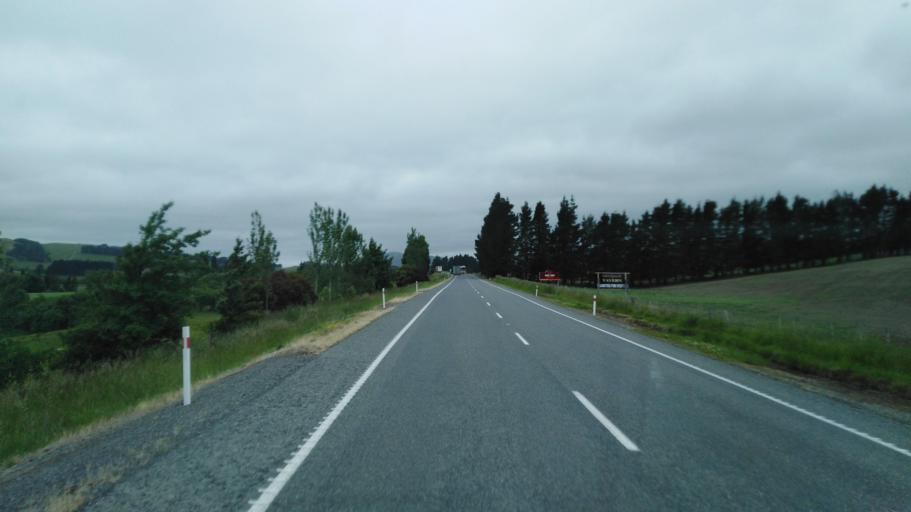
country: NZ
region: Canterbury
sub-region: Hurunui District
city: Amberley
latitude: -42.9568
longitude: 172.9998
